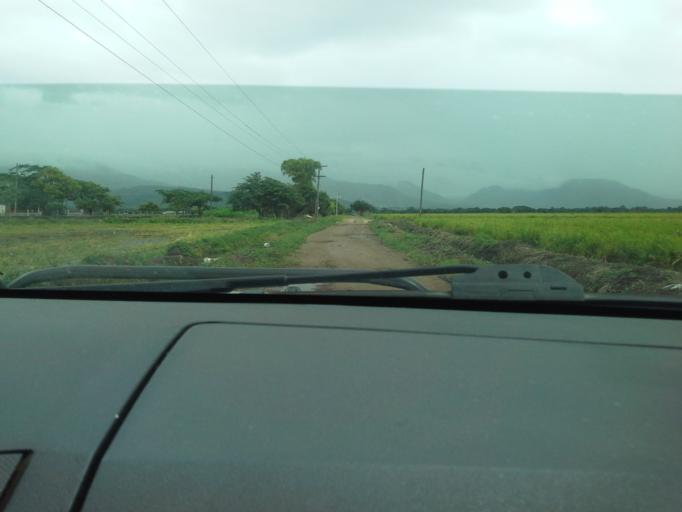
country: NI
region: Matagalpa
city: Ciudad Dario
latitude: 12.8547
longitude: -86.1812
